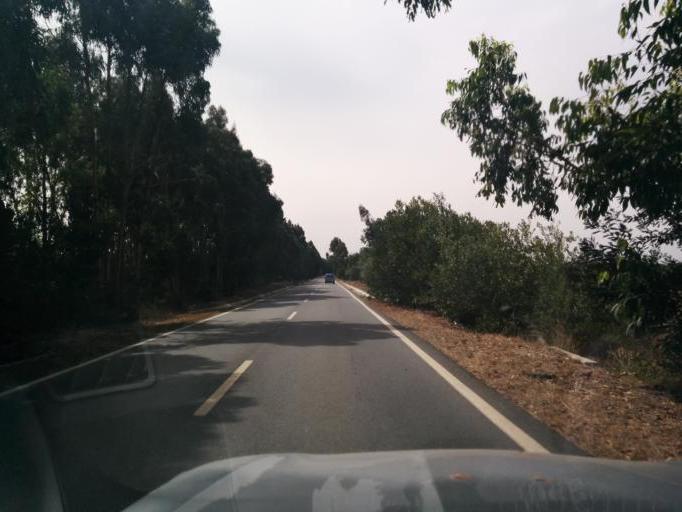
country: PT
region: Beja
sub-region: Odemira
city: Vila Nova de Milfontes
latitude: 37.6768
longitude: -8.7615
